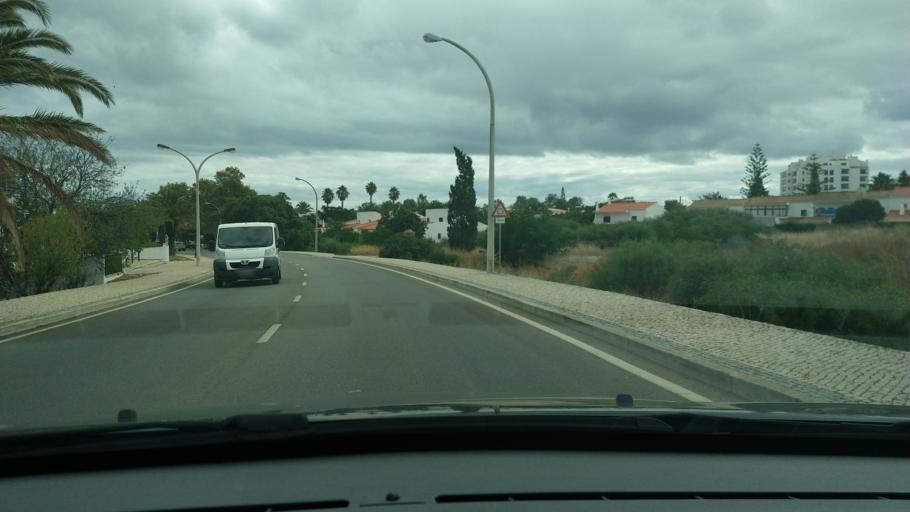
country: PT
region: Faro
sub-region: Lagos
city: Lagos
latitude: 37.0962
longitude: -8.6777
